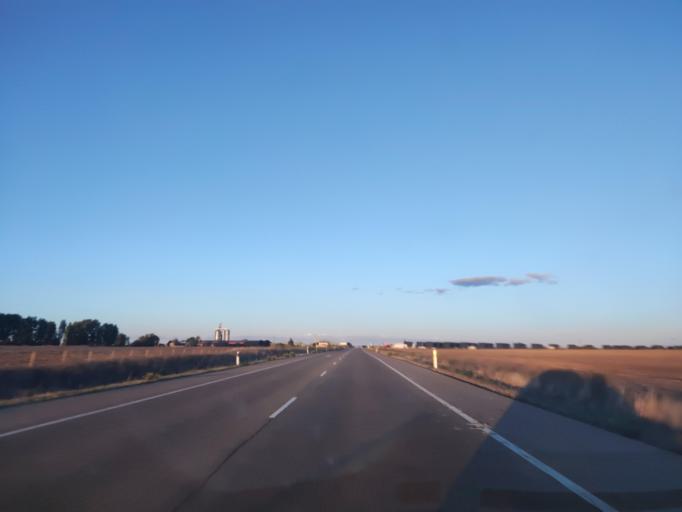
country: ES
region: Castille and Leon
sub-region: Provincia de Salamanca
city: La Fuente de San Esteban
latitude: 40.7868
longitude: -6.2566
